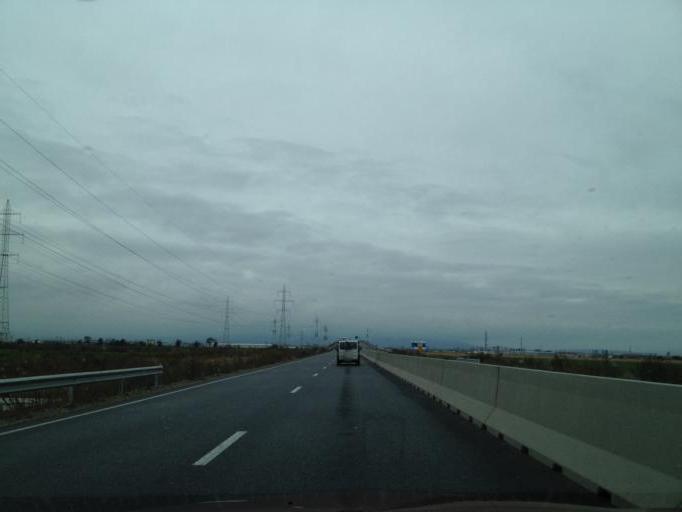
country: RO
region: Brasov
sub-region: Comuna Sanpetru
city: Sanpetru
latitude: 45.6921
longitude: 25.6032
